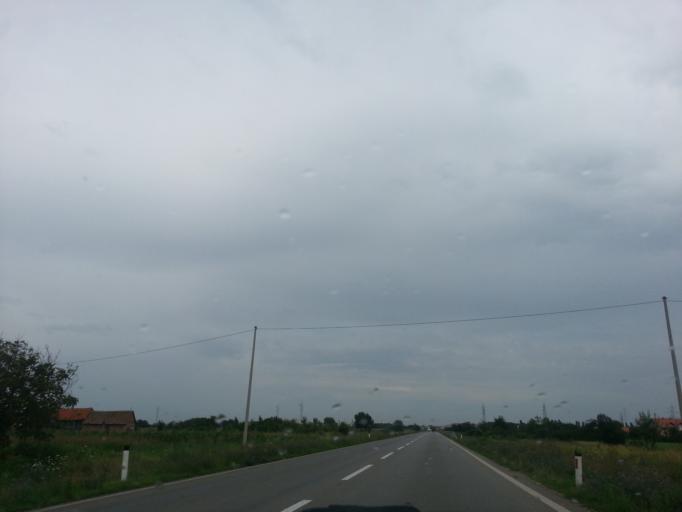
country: BA
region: Republika Srpska
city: Bijeljina
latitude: 44.7746
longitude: 19.2042
